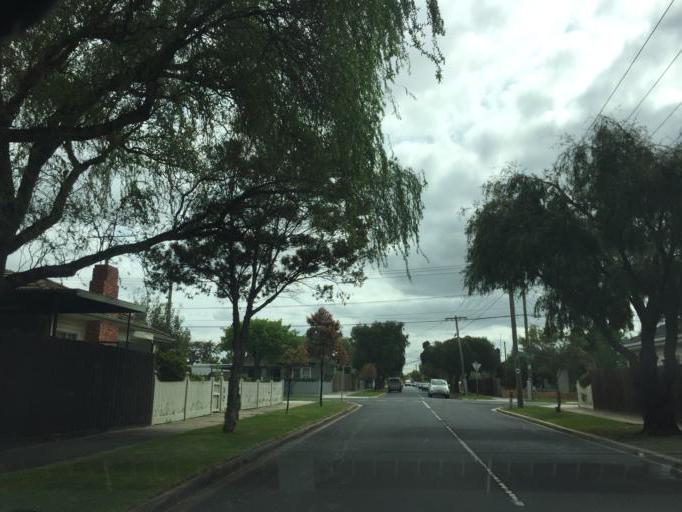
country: AU
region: Victoria
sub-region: Hobsons Bay
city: South Kingsville
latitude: -37.8169
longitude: 144.8664
